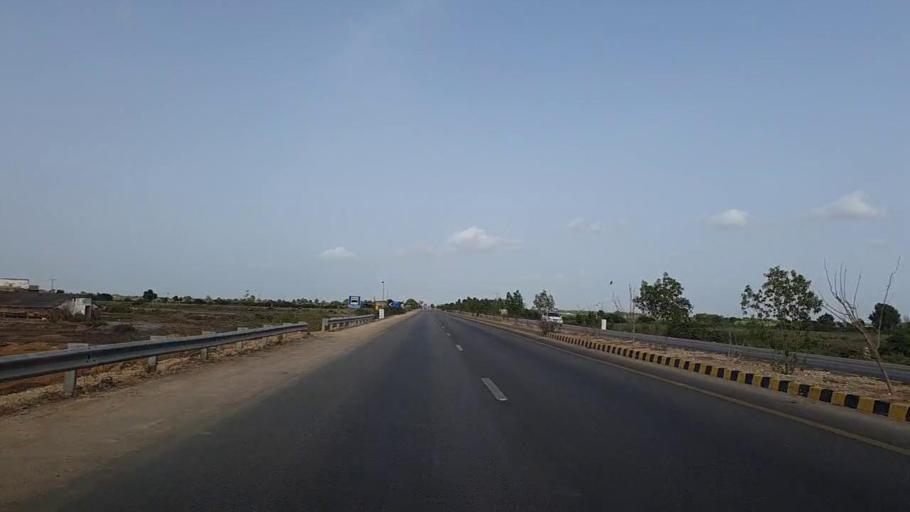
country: PK
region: Sindh
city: Gharo
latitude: 24.7320
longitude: 67.6699
